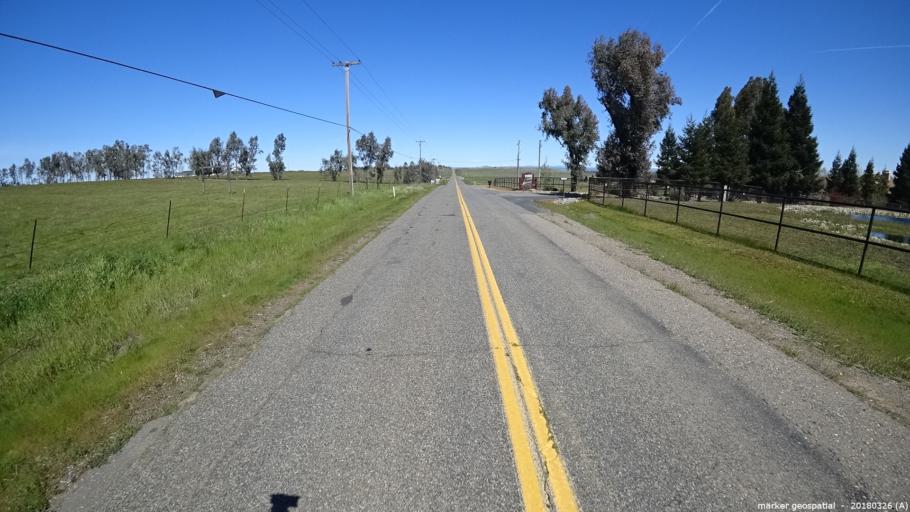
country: US
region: California
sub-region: Sacramento County
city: Wilton
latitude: 38.4841
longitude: -121.2186
